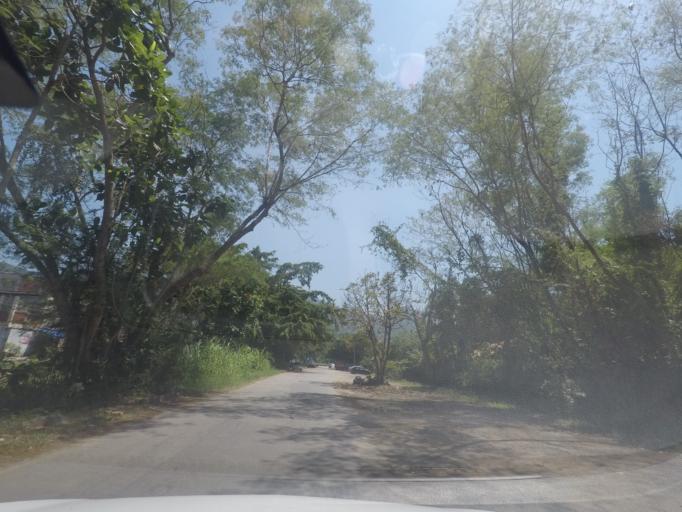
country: BR
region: Rio de Janeiro
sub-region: Nilopolis
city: Nilopolis
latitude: -22.9897
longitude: -43.4555
